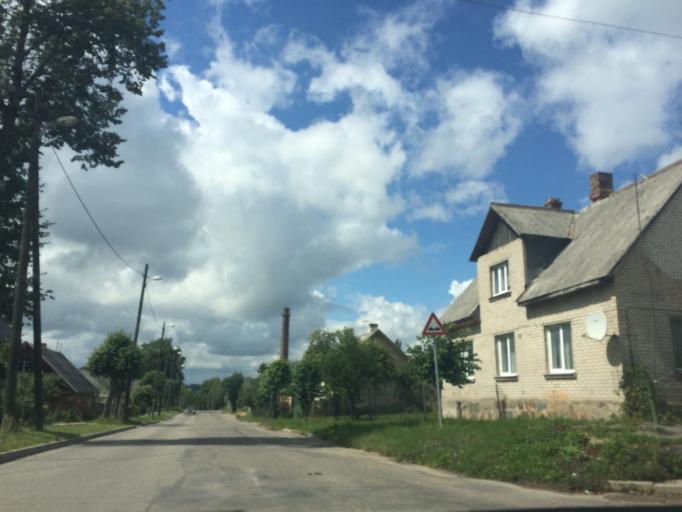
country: LV
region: Rezekne
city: Rezekne
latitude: 56.5090
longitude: 27.3291
